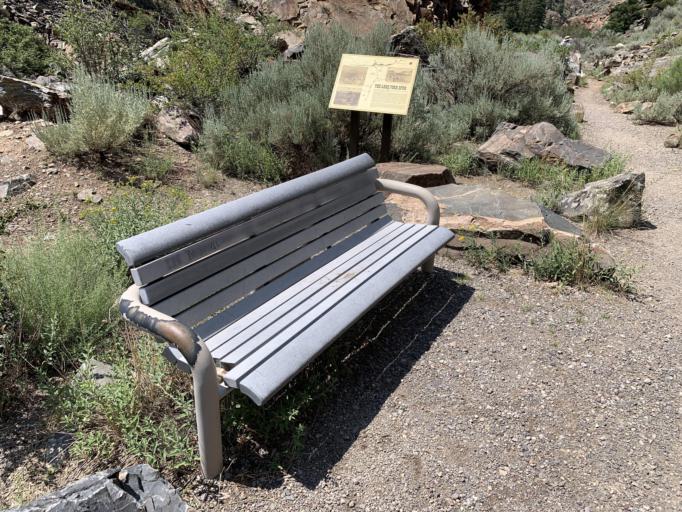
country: US
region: Colorado
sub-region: Gunnison County
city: Gunnison
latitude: 38.3848
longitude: -107.2438
